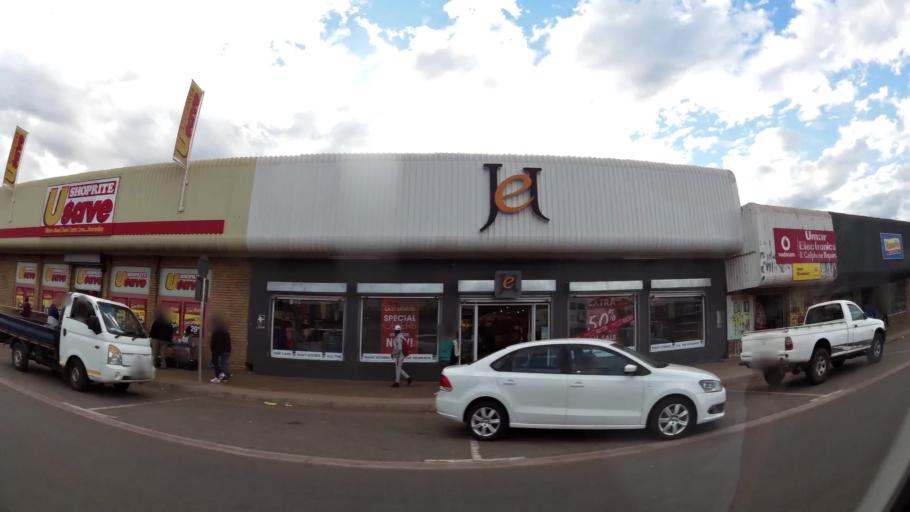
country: ZA
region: Limpopo
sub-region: Waterberg District Municipality
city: Modimolle
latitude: -24.5182
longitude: 28.7156
